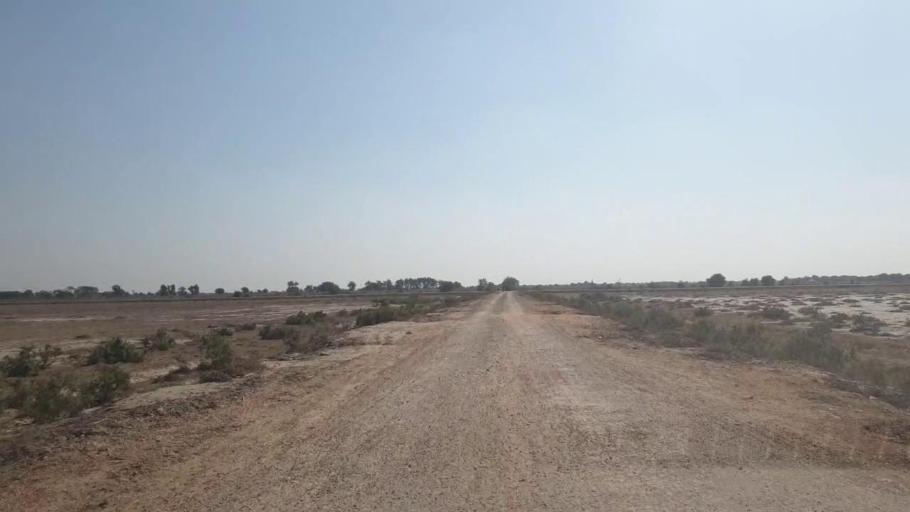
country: PK
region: Sindh
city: Chambar
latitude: 25.2971
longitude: 68.7418
